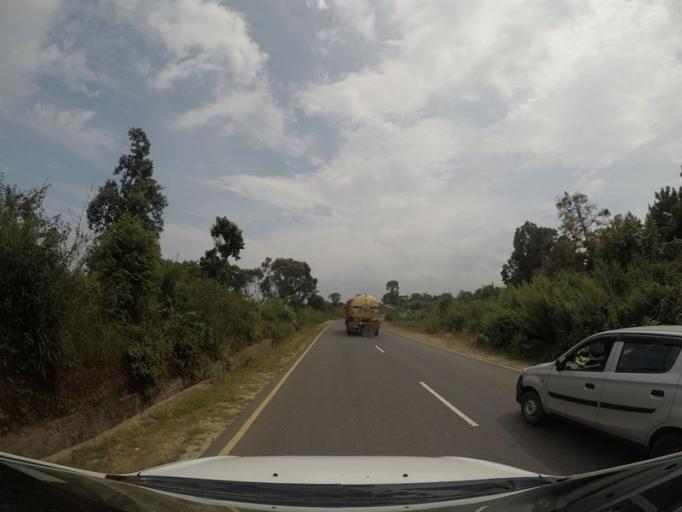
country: IN
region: Meghalaya
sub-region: East Khasi Hills
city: Shillong
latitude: 25.4883
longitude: 92.1911
